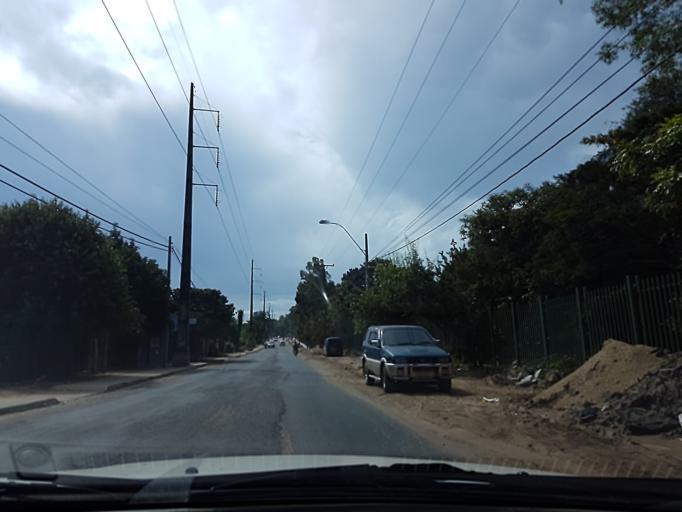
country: PY
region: Asuncion
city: Asuncion
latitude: -25.2502
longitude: -57.5798
